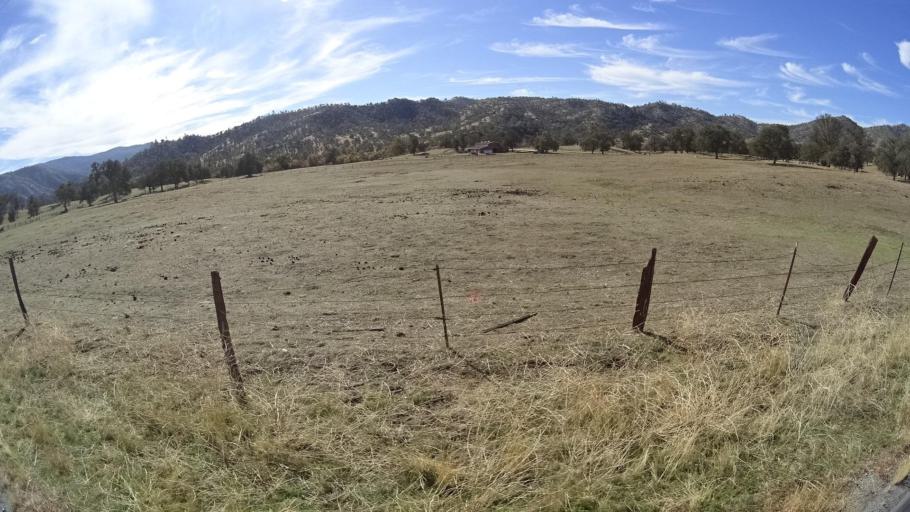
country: US
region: California
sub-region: Kern County
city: Alta Sierra
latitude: 35.6205
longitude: -118.7346
